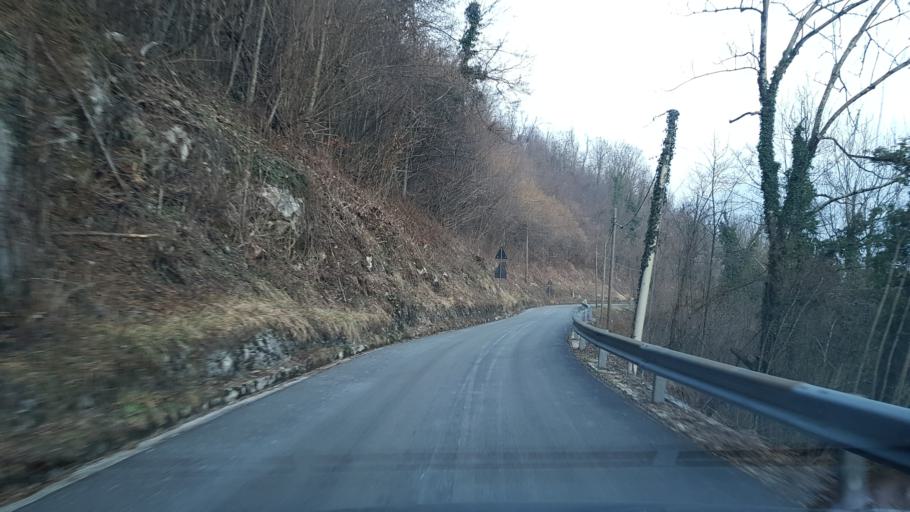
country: IT
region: Friuli Venezia Giulia
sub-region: Provincia di Udine
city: Taipana
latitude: 46.2388
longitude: 13.3932
